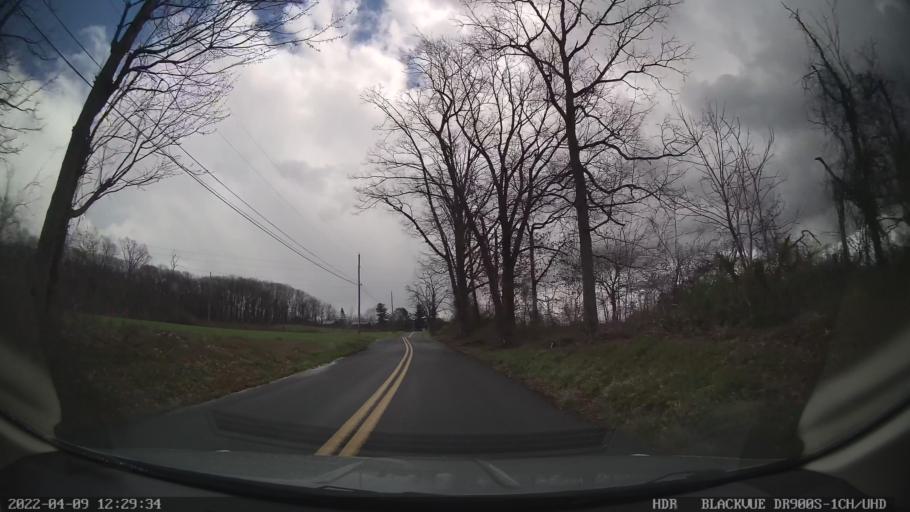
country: US
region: Pennsylvania
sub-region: Berks County
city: Kutztown
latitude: 40.4671
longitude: -75.7656
